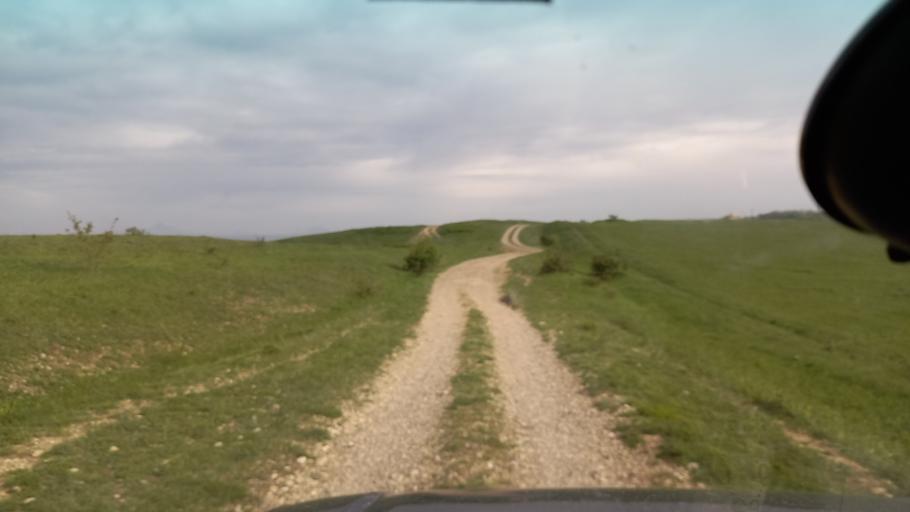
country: RU
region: Kabardino-Balkariya
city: Kuba-Taba
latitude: 43.8071
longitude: 43.4079
